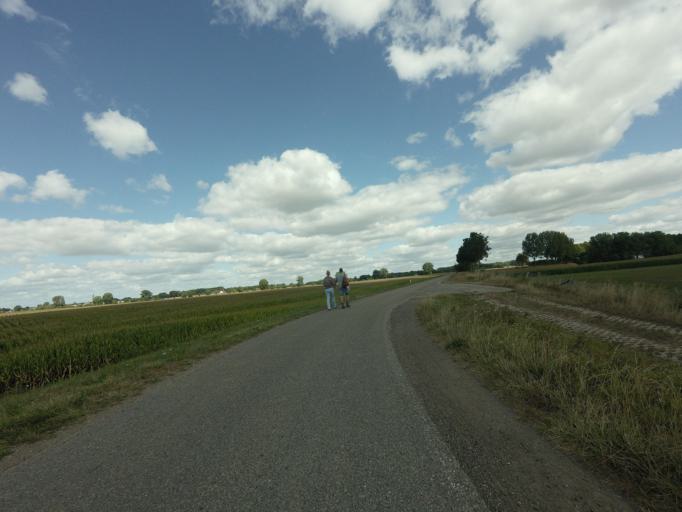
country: NL
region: North Brabant
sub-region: Gemeente Oss
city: Berghem
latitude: 51.8214
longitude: 5.5950
